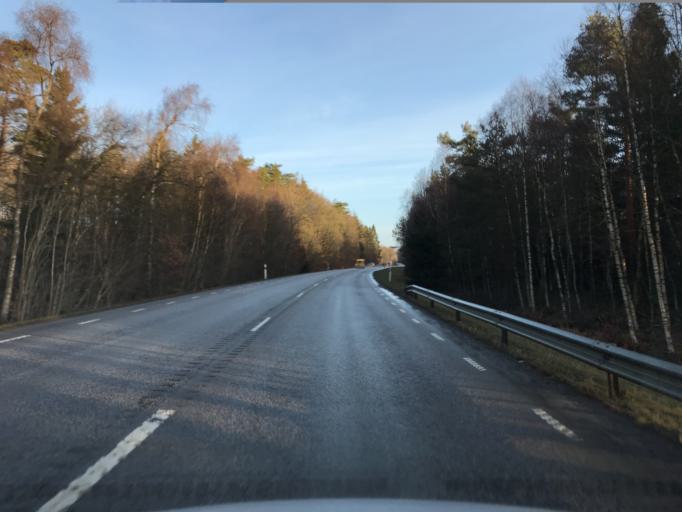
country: SE
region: Skane
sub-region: Hassleholms Kommun
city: Bjarnum
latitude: 56.2597
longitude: 13.7177
